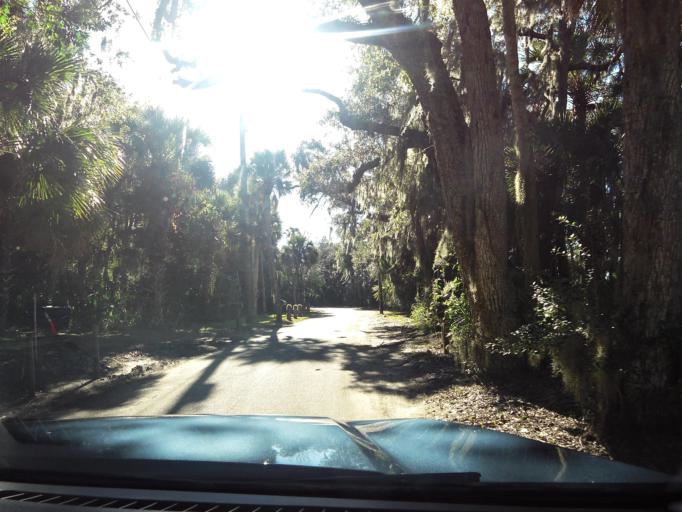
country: US
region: Florida
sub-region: Duval County
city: Atlantic Beach
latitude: 30.4054
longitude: -81.4316
